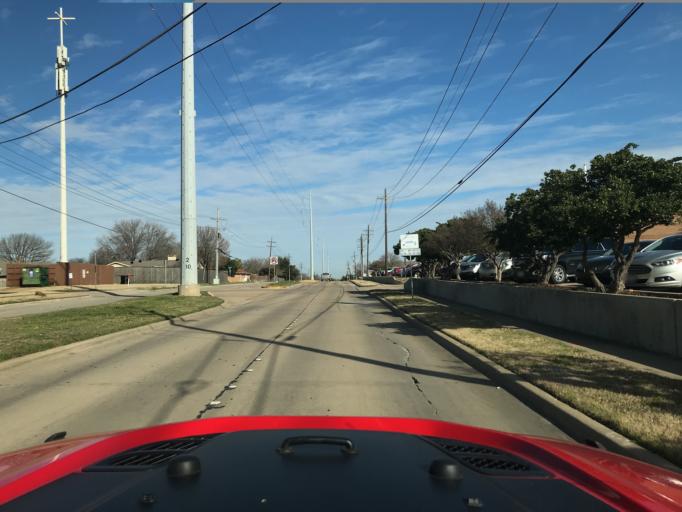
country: US
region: Texas
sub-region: Denton County
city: Lewisville
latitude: 33.0434
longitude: -97.0359
